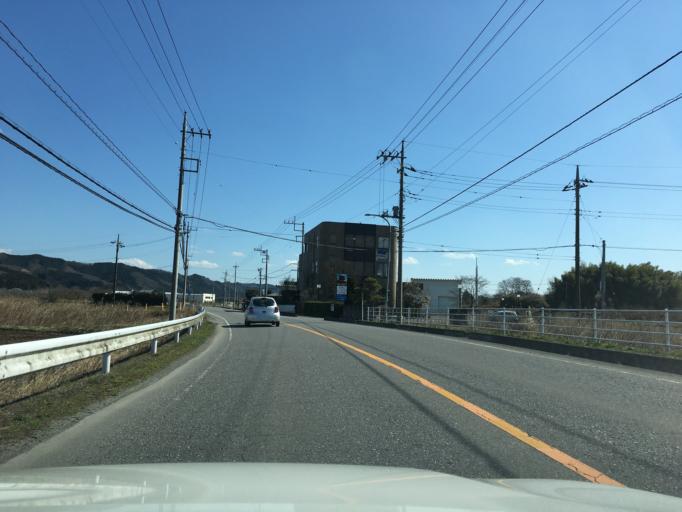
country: JP
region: Tochigi
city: Karasuyama
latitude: 36.7259
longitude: 140.1429
